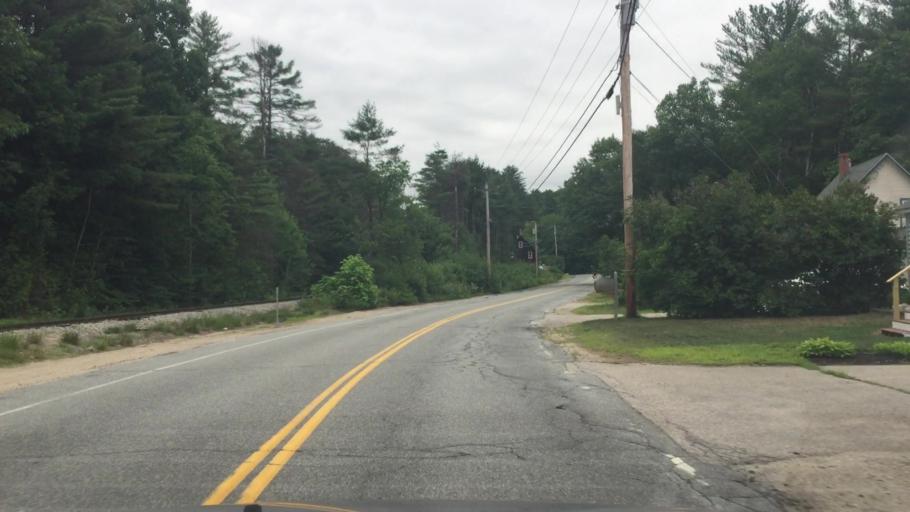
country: US
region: New Hampshire
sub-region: Carroll County
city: North Conway
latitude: 44.0922
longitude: -71.2025
